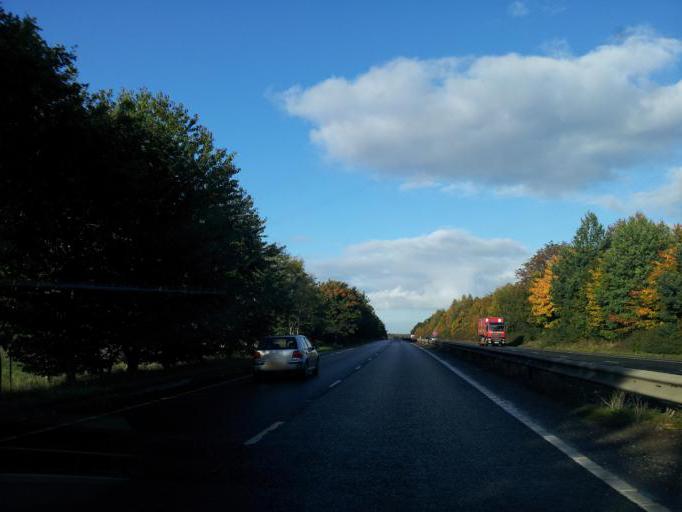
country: GB
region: England
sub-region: Norfolk
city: Costessey
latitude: 52.6545
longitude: 1.1642
